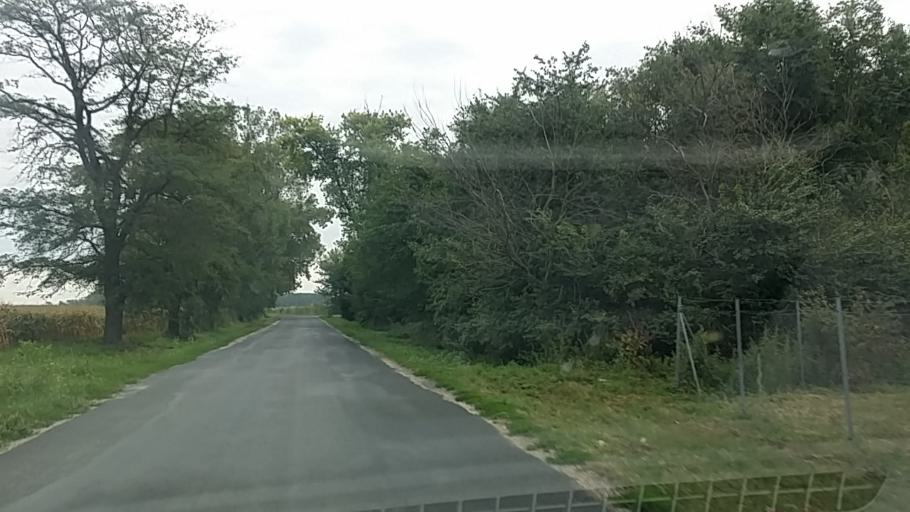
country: HU
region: Gyor-Moson-Sopron
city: Kapuvar
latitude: 47.6415
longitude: 17.0820
